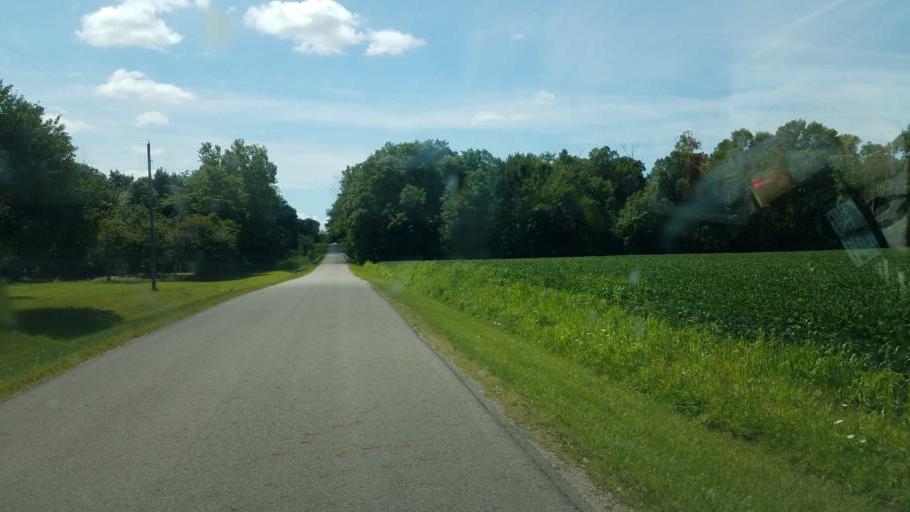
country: US
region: Ohio
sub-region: Knox County
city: Centerburg
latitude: 40.3576
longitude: -82.7922
